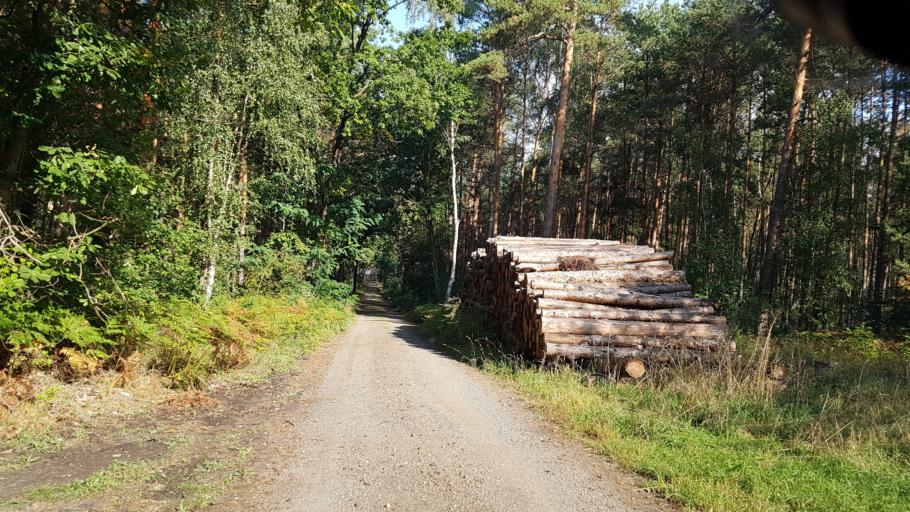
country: DE
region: Brandenburg
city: Plessa
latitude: 51.5241
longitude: 13.6388
